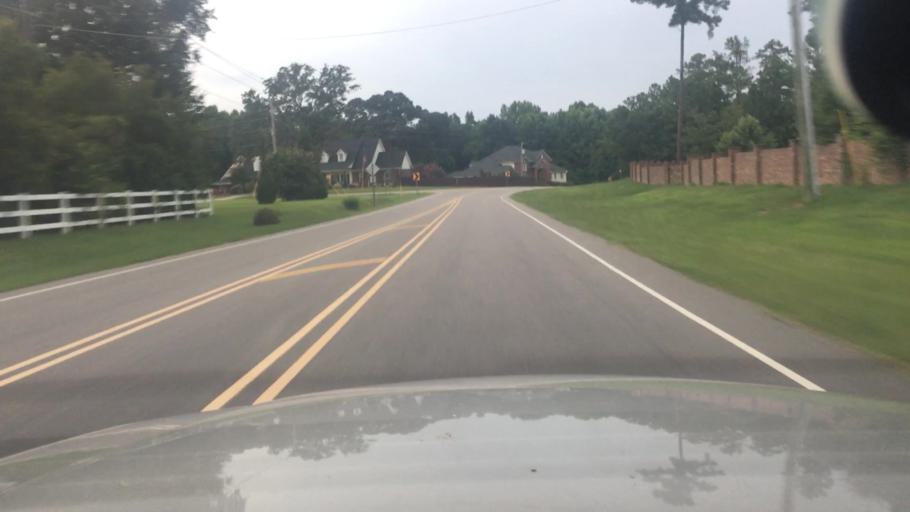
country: US
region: North Carolina
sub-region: Hoke County
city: Rockfish
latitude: 35.0015
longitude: -79.0258
